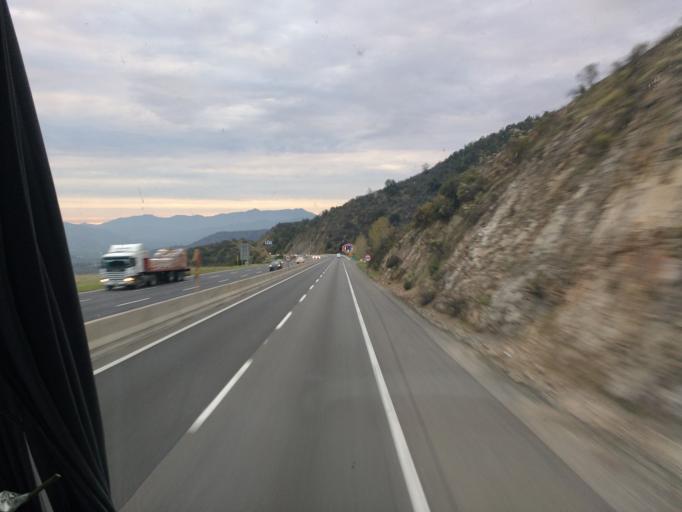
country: CL
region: Santiago Metropolitan
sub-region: Provincia de Talagante
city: Penaflor
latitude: -33.4570
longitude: -70.9681
